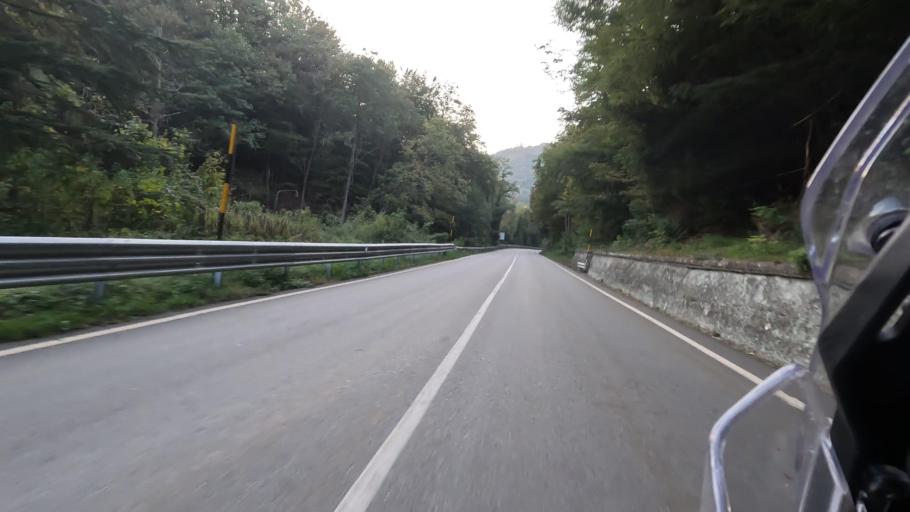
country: IT
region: Liguria
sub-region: Provincia di Savona
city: Osteria dei Cacciatori-Stella
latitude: 44.4460
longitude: 8.4810
